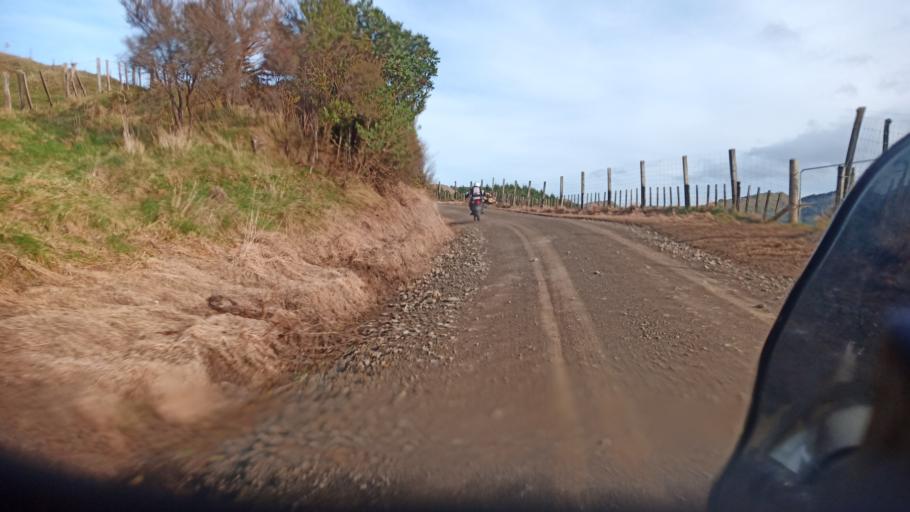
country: NZ
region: Bay of Plenty
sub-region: Opotiki District
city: Opotiki
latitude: -38.4481
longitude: 177.5393
